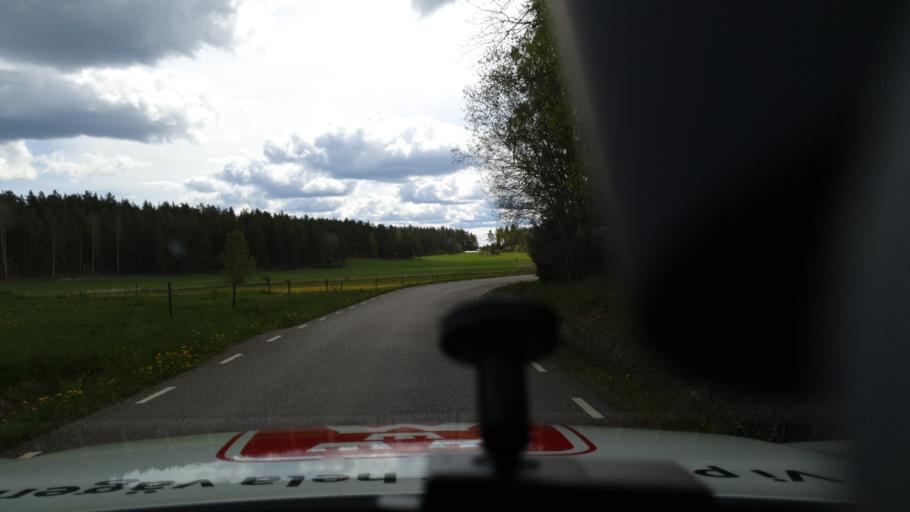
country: SE
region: Kalmar
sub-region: Vasterviks Kommun
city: Forserum
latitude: 57.9270
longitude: 16.4552
